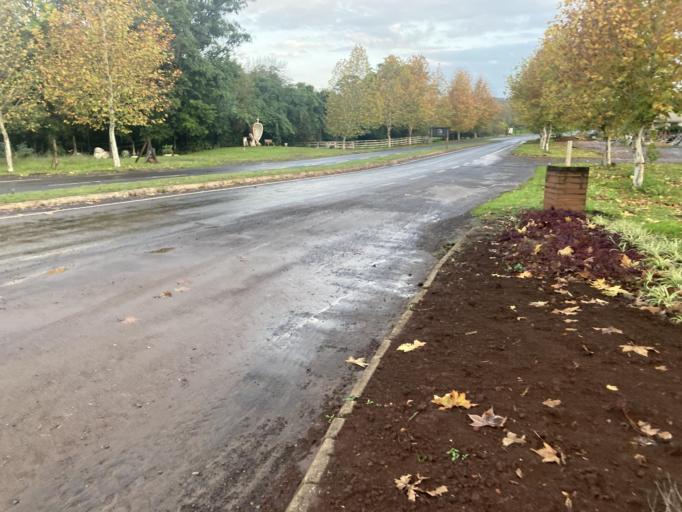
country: BR
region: Rio Grande do Sul
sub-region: Sao Pedro Do Butia
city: Butia Inferior
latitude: -27.9902
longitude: -54.8324
